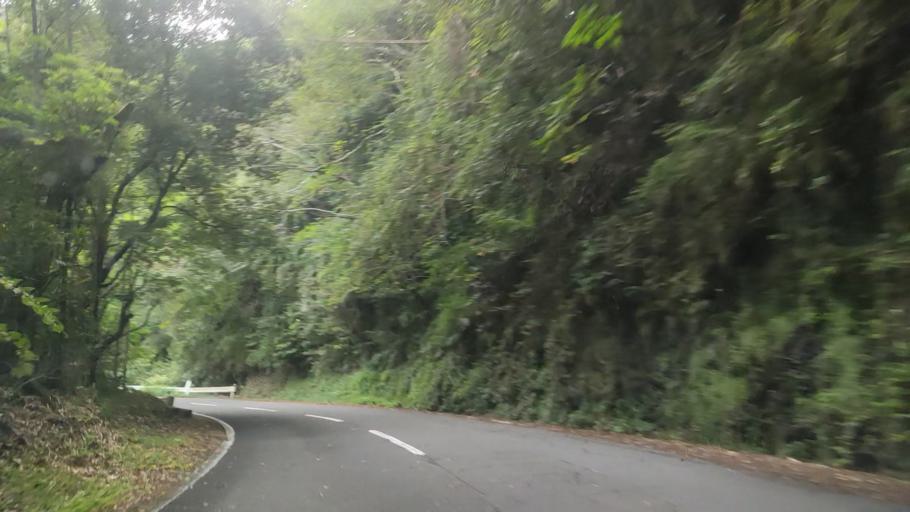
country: JP
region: Wakayama
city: Koya
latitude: 34.2560
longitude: 135.5429
